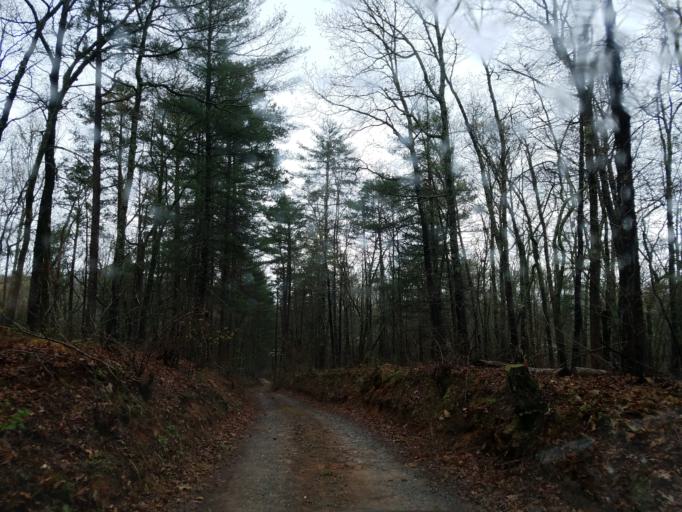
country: US
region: Georgia
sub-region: Fannin County
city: Blue Ridge
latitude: 34.8305
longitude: -84.2381
